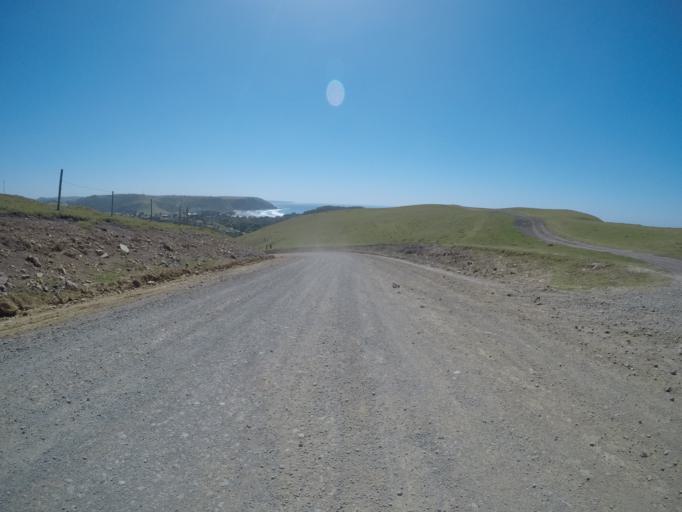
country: ZA
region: Eastern Cape
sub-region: OR Tambo District Municipality
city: Libode
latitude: -31.9909
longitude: 29.1443
